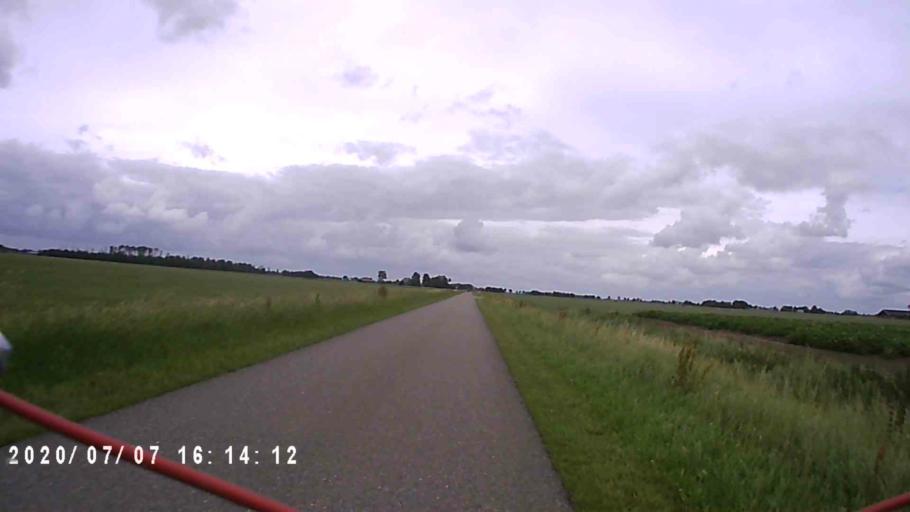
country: NL
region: Groningen
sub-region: Gemeente Winsum
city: Winsum
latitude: 53.3738
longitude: 6.5431
